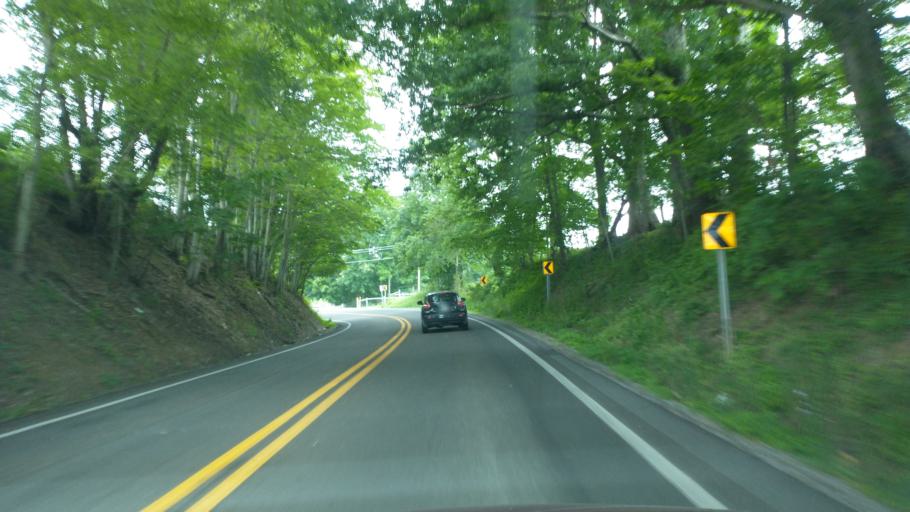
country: US
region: West Virginia
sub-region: Mercer County
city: Athens
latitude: 37.4092
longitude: -81.0280
